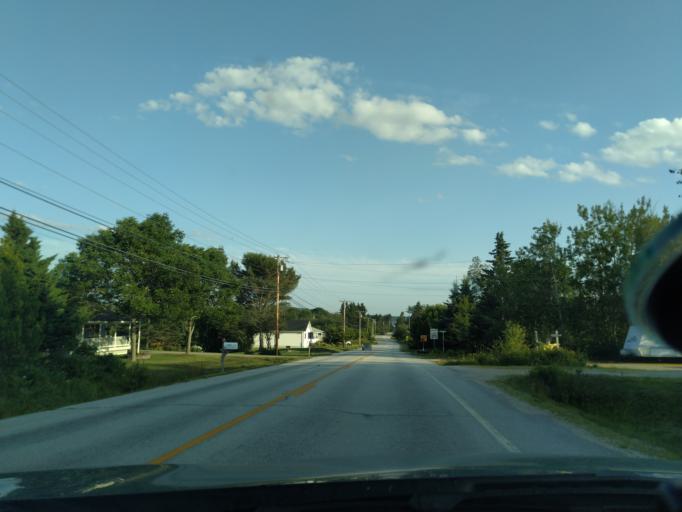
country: US
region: Maine
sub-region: Hancock County
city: Gouldsboro
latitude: 44.4013
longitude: -68.0864
